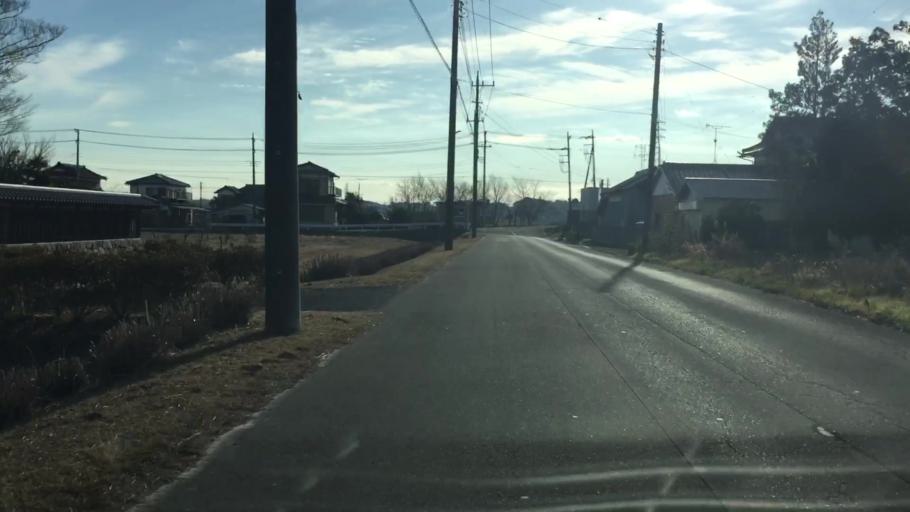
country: JP
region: Ibaraki
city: Toride
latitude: 35.8420
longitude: 140.1297
